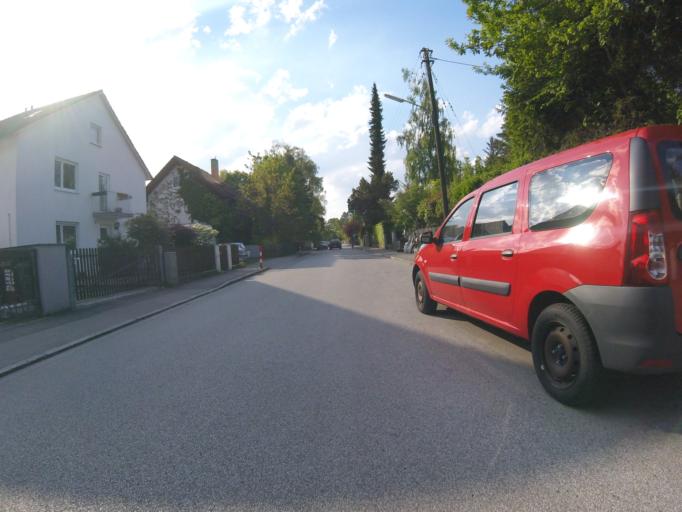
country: DE
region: Bavaria
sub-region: Upper Bavaria
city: Ottobrunn
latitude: 48.0591
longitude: 11.6832
